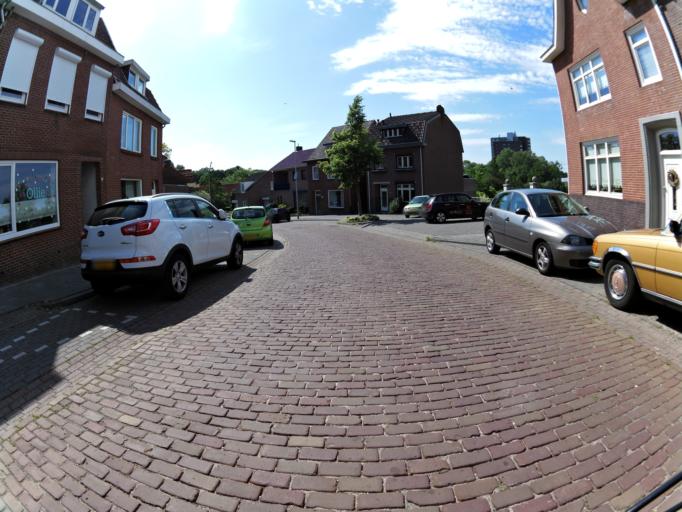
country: NL
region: Limburg
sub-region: Gemeente Heerlen
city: Heerlen
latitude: 50.9026
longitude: 5.9824
